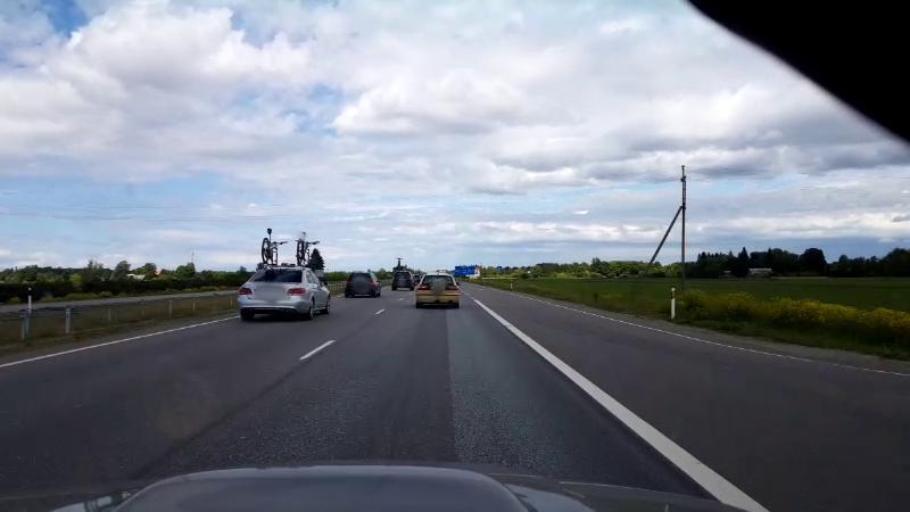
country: EE
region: Harju
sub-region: Saue linn
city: Saue
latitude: 59.3056
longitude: 24.5643
